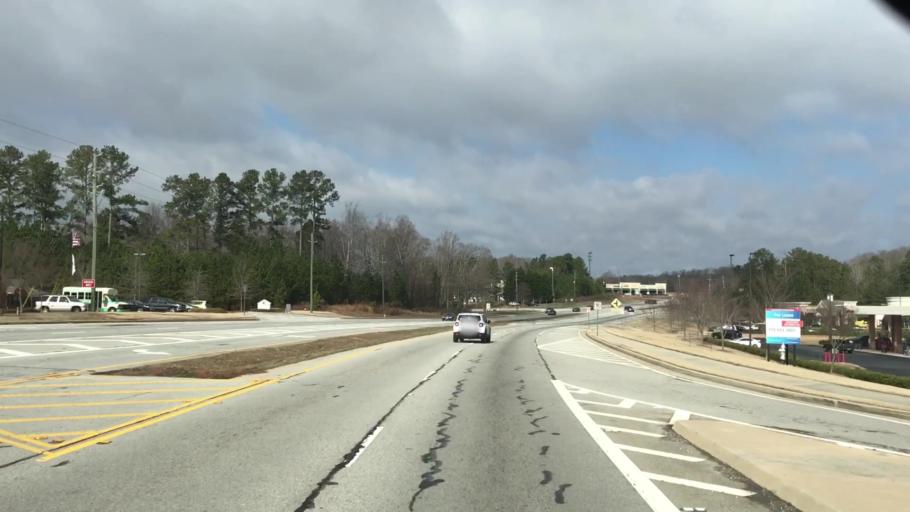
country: US
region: Georgia
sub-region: Hall County
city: Oakwood
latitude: 34.1959
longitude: -83.8589
